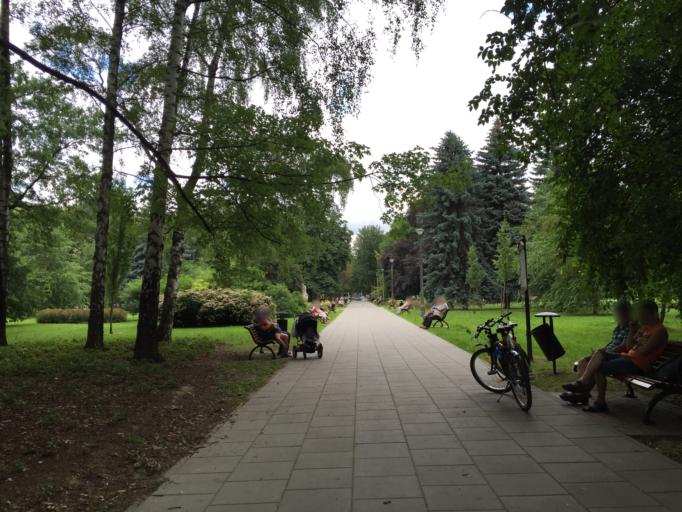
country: PL
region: Lesser Poland Voivodeship
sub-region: Powiat wielicki
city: Kokotow
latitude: 50.0749
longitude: 20.0397
